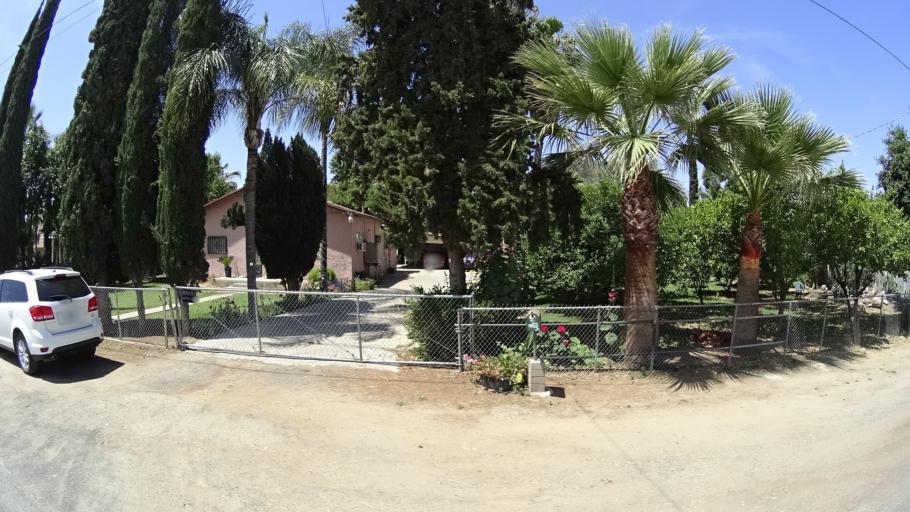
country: US
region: California
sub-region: Kings County
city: Home Garden
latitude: 36.3016
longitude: -119.6460
